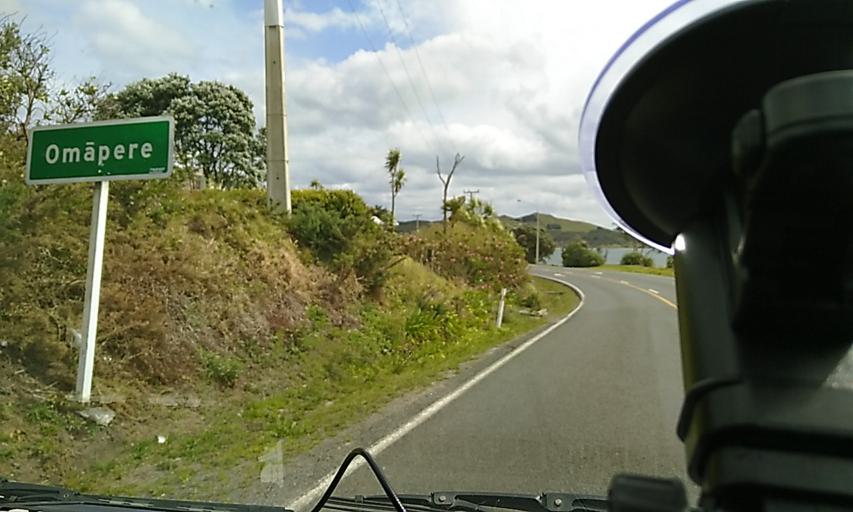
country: NZ
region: Northland
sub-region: Far North District
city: Ahipara
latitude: -35.5181
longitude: 173.3882
